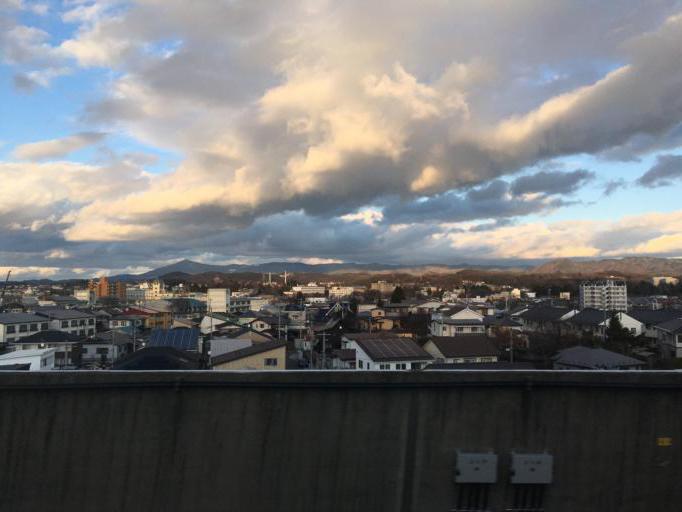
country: JP
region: Iwate
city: Morioka-shi
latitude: 39.7105
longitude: 141.1264
